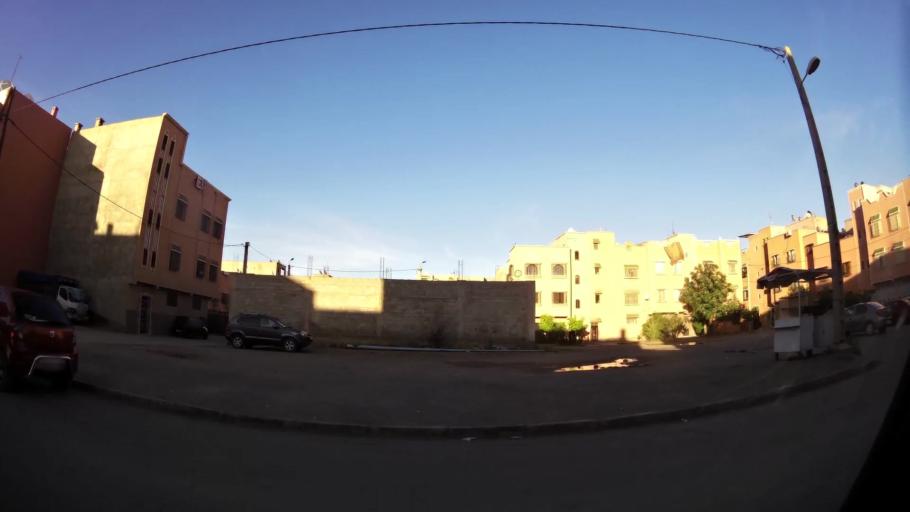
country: MA
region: Marrakech-Tensift-Al Haouz
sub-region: Marrakech
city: Marrakesh
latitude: 31.6196
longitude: -8.0492
